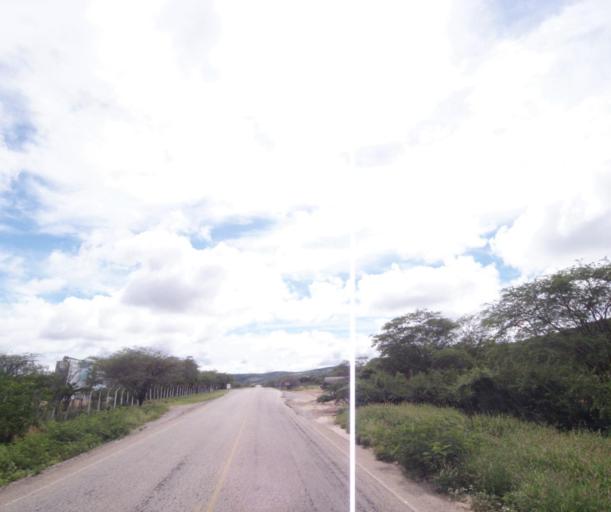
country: BR
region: Bahia
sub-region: Brumado
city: Brumado
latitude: -14.1999
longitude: -41.6027
